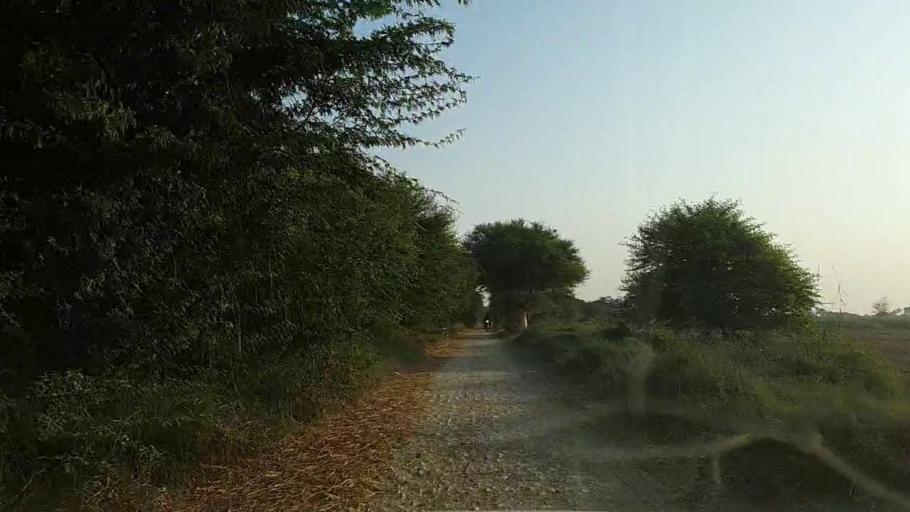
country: PK
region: Sindh
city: Daro Mehar
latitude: 24.7514
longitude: 68.1861
